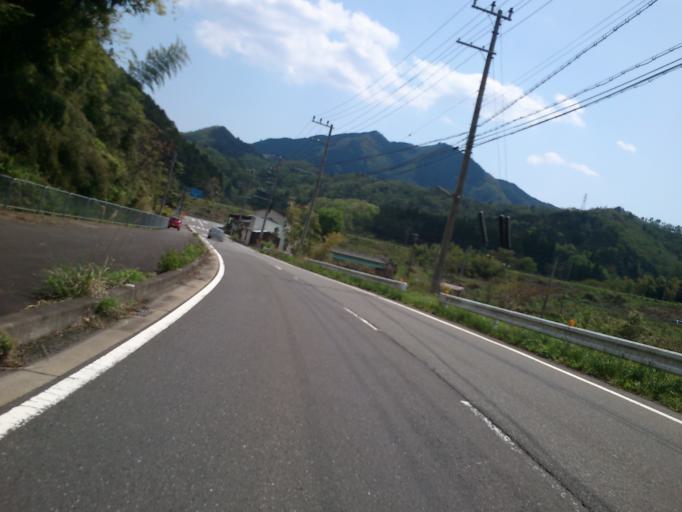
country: JP
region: Kyoto
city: Fukuchiyama
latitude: 35.3308
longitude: 134.9465
